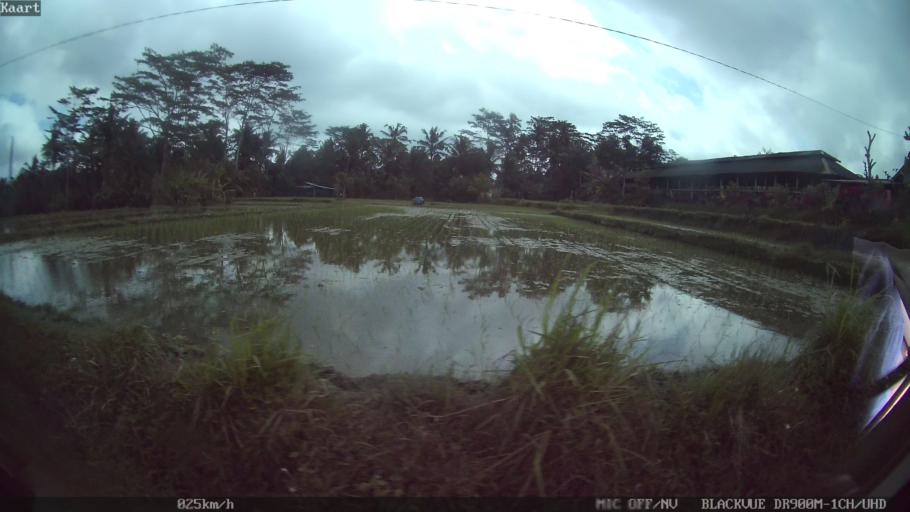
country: ID
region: Bali
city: Banjar Petak
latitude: -8.4427
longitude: 115.3225
